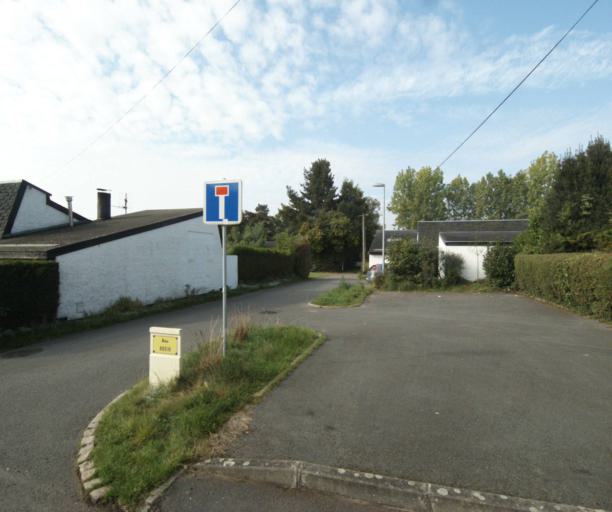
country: FR
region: Nord-Pas-de-Calais
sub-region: Departement du Nord
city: Wattignies
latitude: 50.5840
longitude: 3.0348
